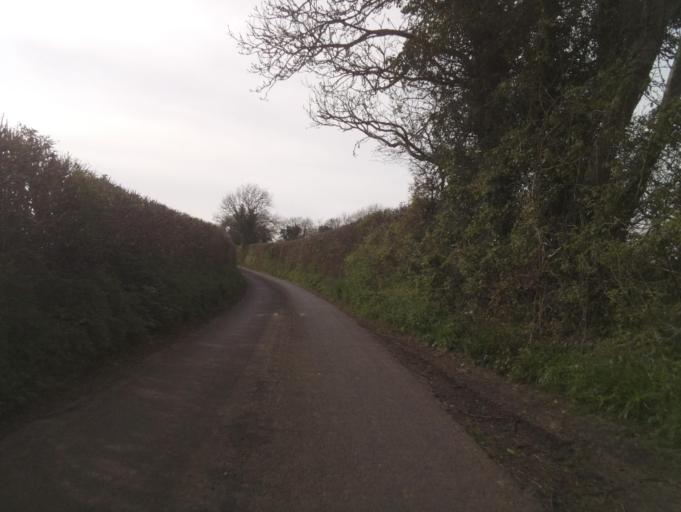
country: GB
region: England
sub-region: Somerset
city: Milborne Port
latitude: 50.9994
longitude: -2.4858
